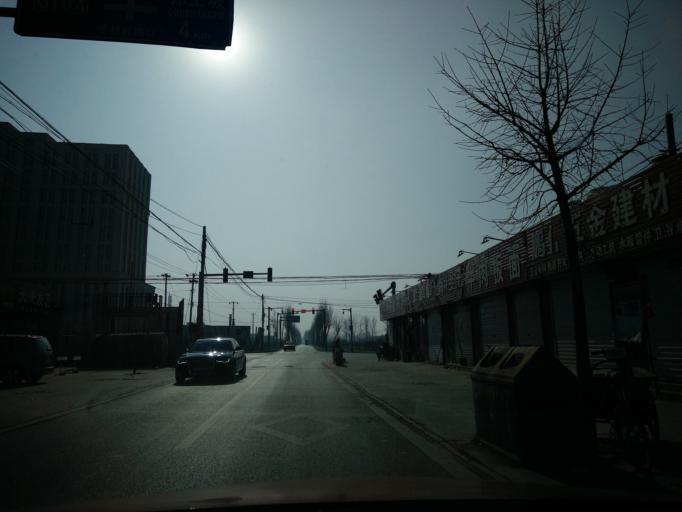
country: CN
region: Beijing
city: Yinghai
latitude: 39.7078
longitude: 116.4576
